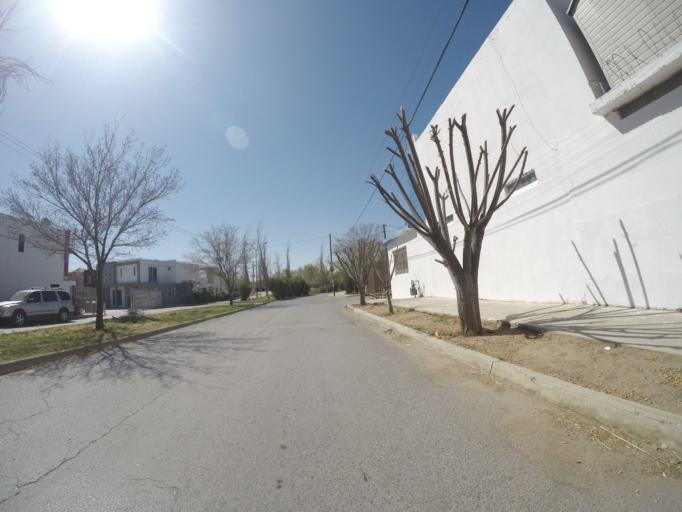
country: MX
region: Chihuahua
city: Ciudad Juarez
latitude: 31.6949
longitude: -106.4152
